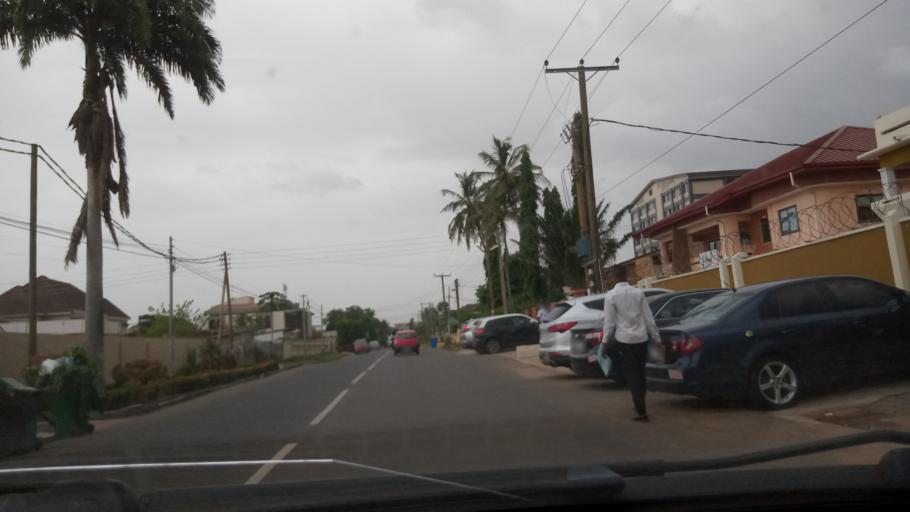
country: GH
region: Greater Accra
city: Dome
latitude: 5.6160
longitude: -0.1981
